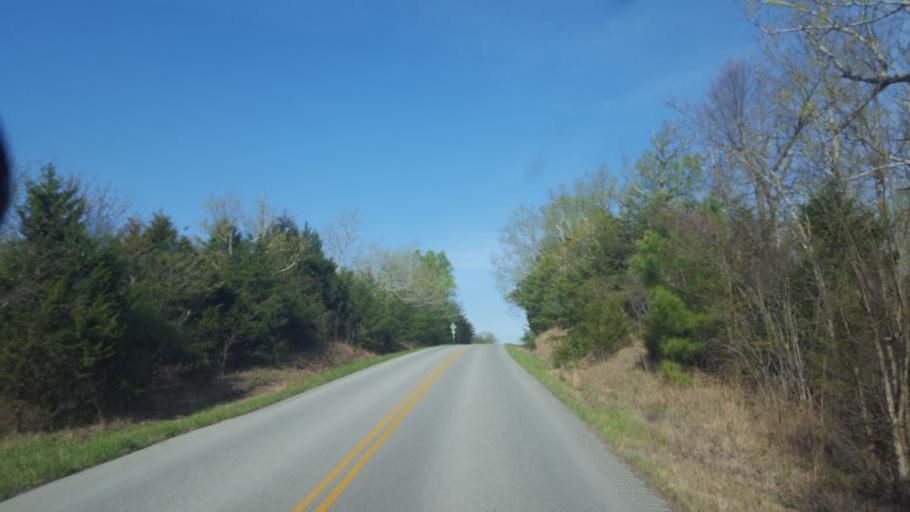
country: US
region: Kentucky
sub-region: Hart County
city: Munfordville
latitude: 37.3149
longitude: -86.0762
